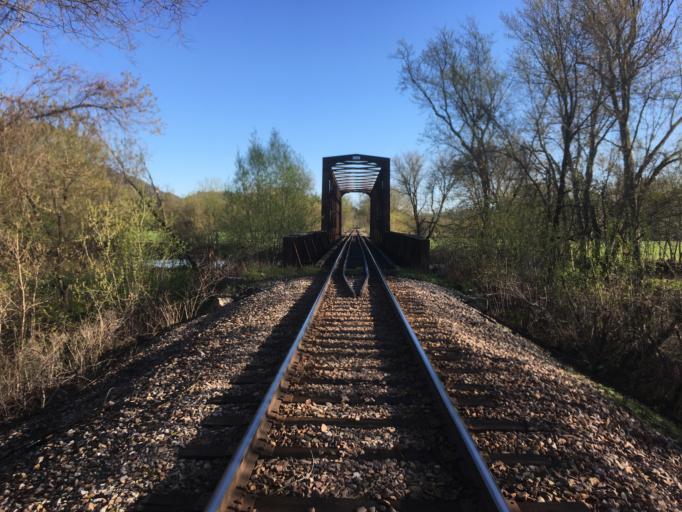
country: US
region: Vermont
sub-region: Rutland County
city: West Rutland
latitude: 43.6417
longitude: -73.0363
